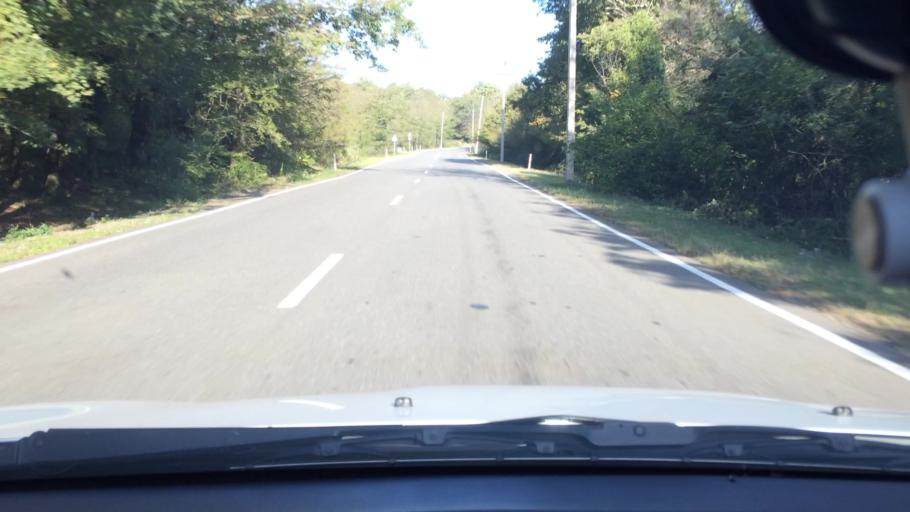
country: GE
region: Imereti
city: Kutaisi
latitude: 42.2465
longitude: 42.7576
